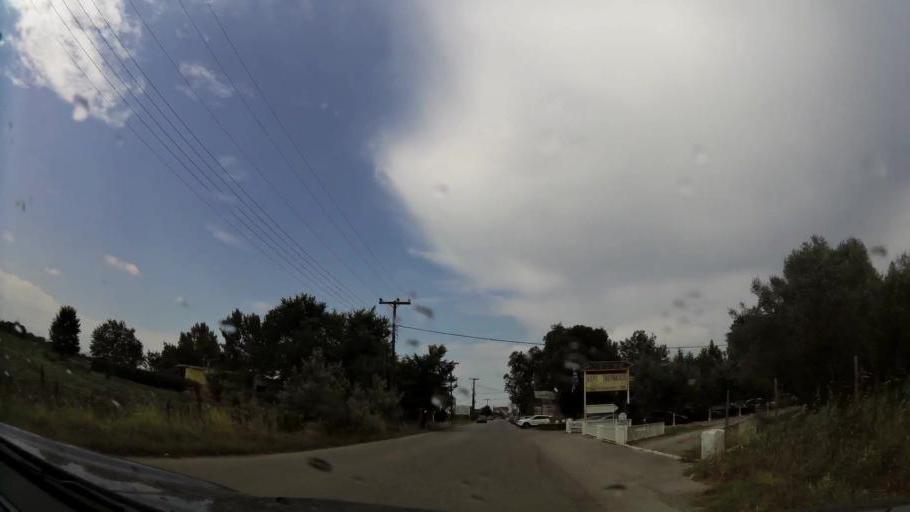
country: GR
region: Central Macedonia
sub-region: Nomos Pierias
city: Korinos
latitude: 40.3016
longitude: 22.6127
